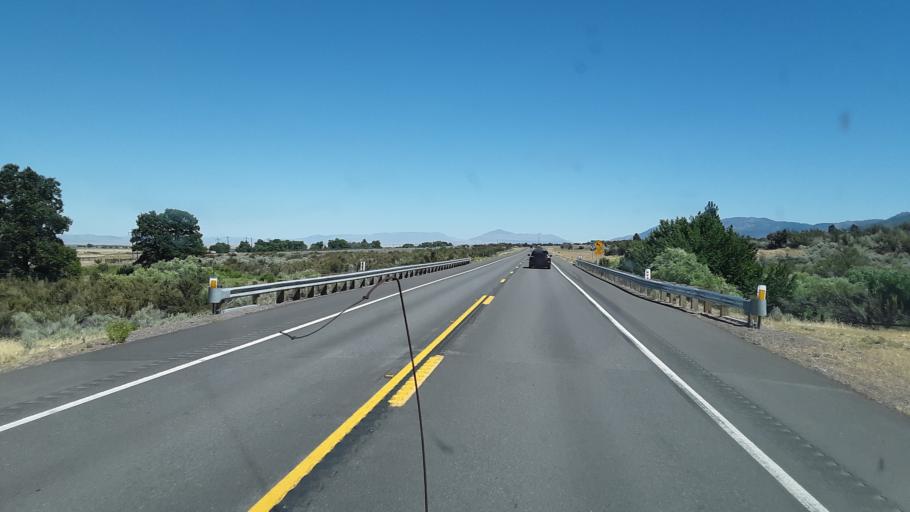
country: US
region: California
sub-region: Lassen County
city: Janesville
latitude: 40.2883
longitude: -120.4969
